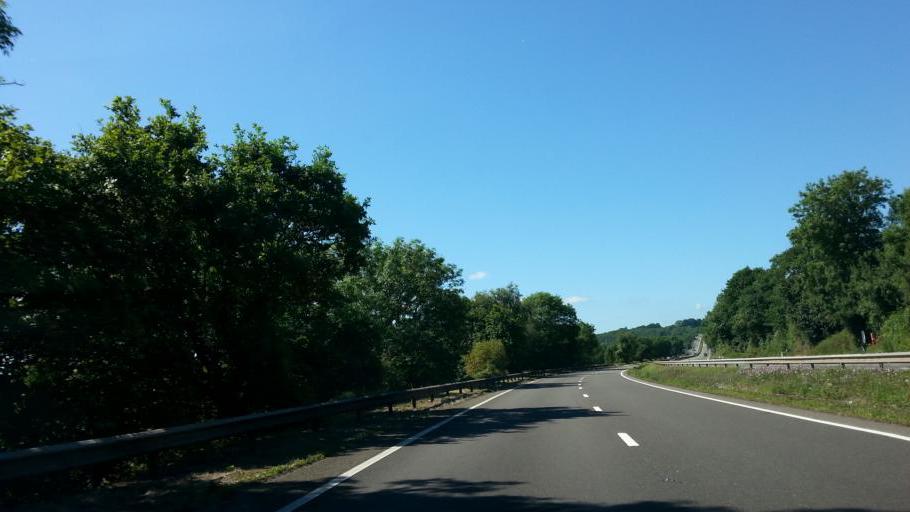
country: GB
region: England
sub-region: Herefordshire
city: Walford
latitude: 51.9039
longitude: -2.6245
